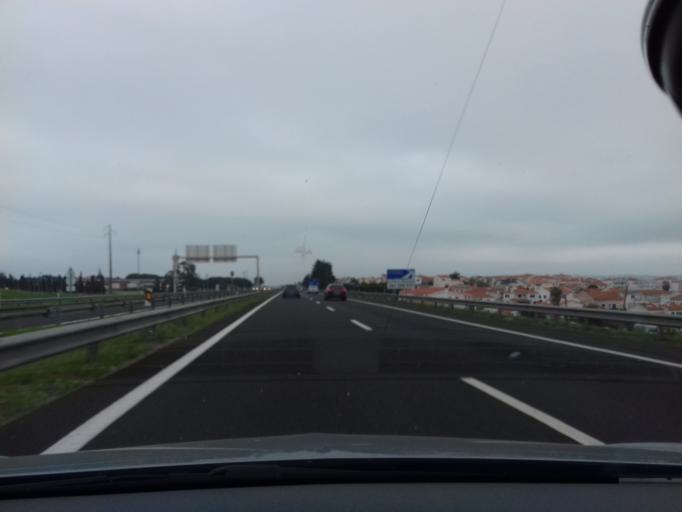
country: PT
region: Leiria
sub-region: Bombarral
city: Bombarral
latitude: 39.2600
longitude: -9.1650
